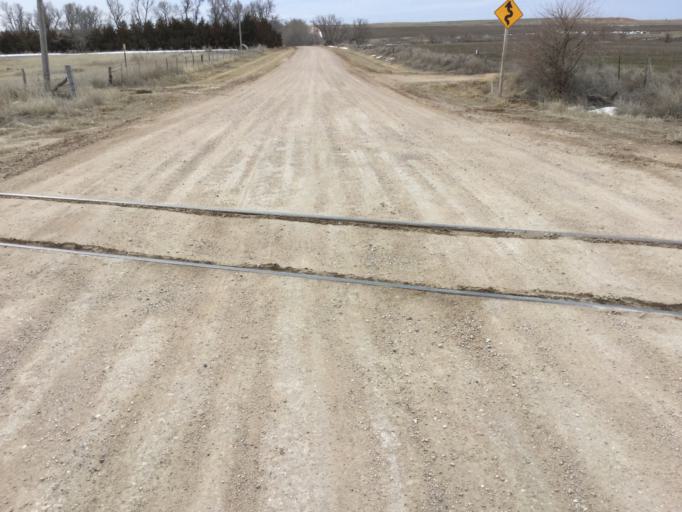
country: US
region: Kansas
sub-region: Lane County
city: Dighton
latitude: 38.4642
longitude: -100.3568
